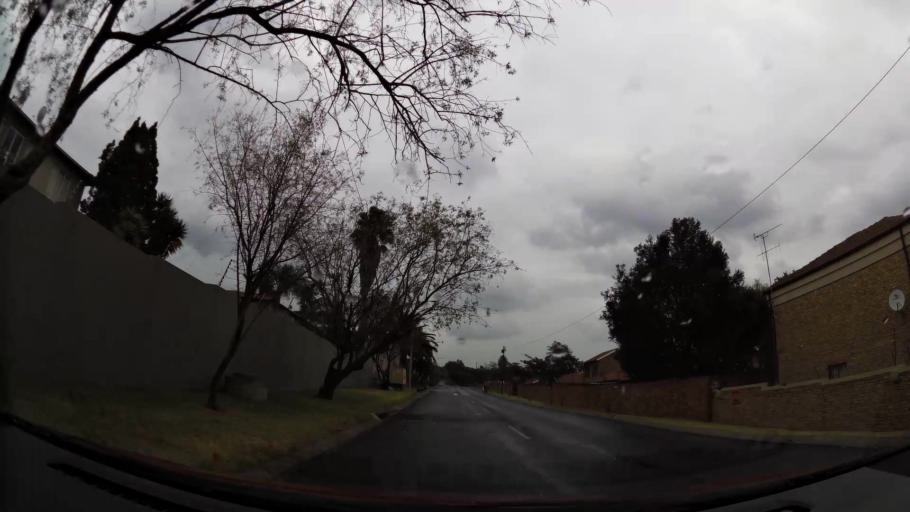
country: ZA
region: Gauteng
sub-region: City of Johannesburg Metropolitan Municipality
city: Roodepoort
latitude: -26.0990
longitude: 27.9218
